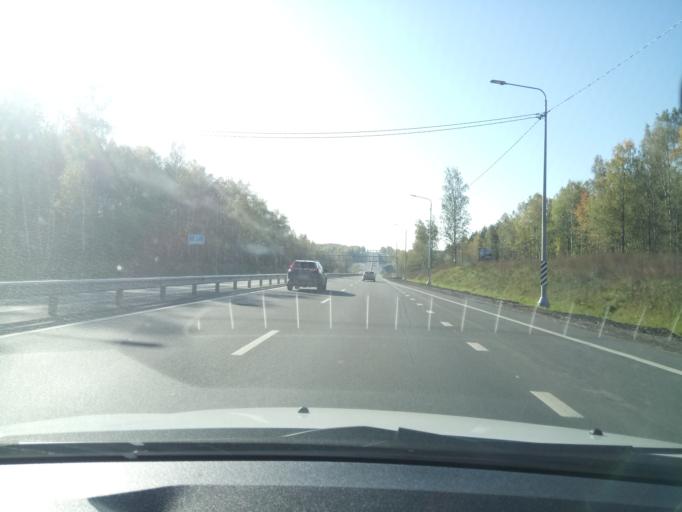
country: RU
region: Nizjnij Novgorod
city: Burevestnik
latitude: 56.0141
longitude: 43.9648
